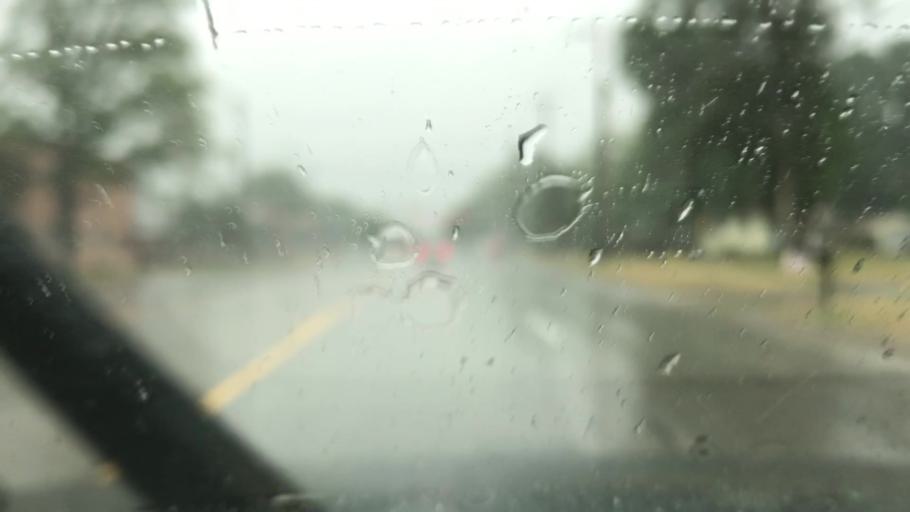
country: US
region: Michigan
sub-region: Kent County
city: Wyoming
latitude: 42.8861
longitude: -85.7242
